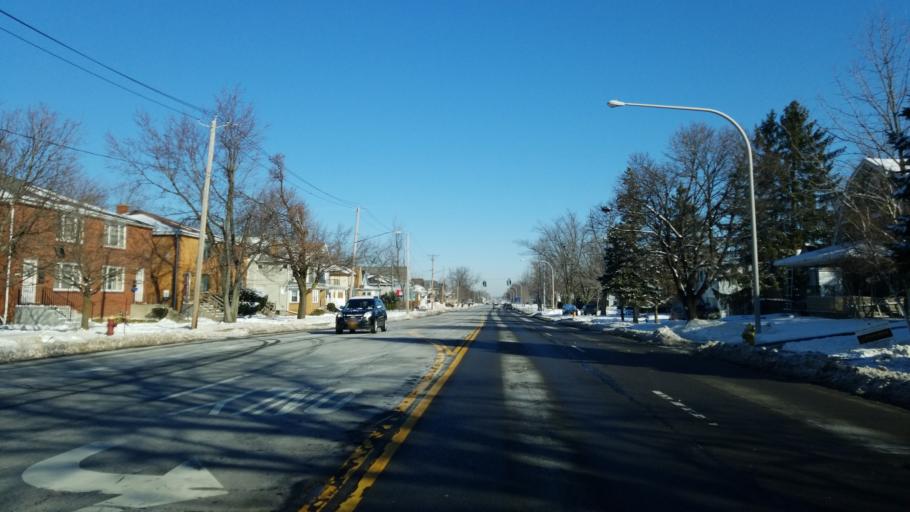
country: US
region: New York
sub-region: Erie County
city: Eggertsville
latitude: 42.9593
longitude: -78.8238
